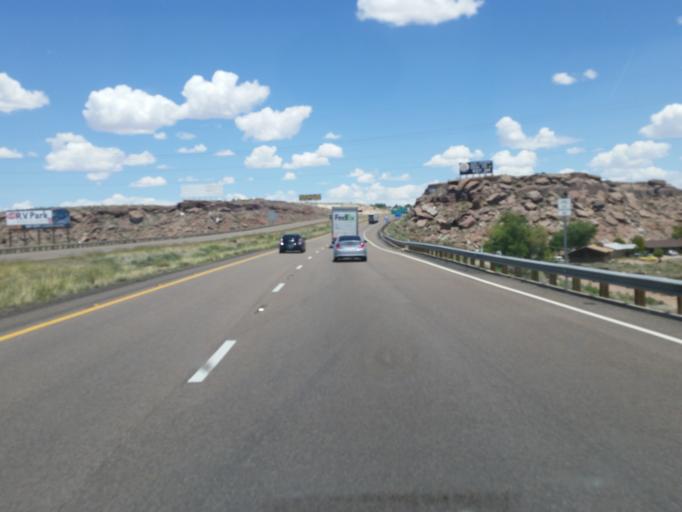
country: US
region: Arizona
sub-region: Navajo County
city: Holbrook
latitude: 34.9088
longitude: -110.1780
